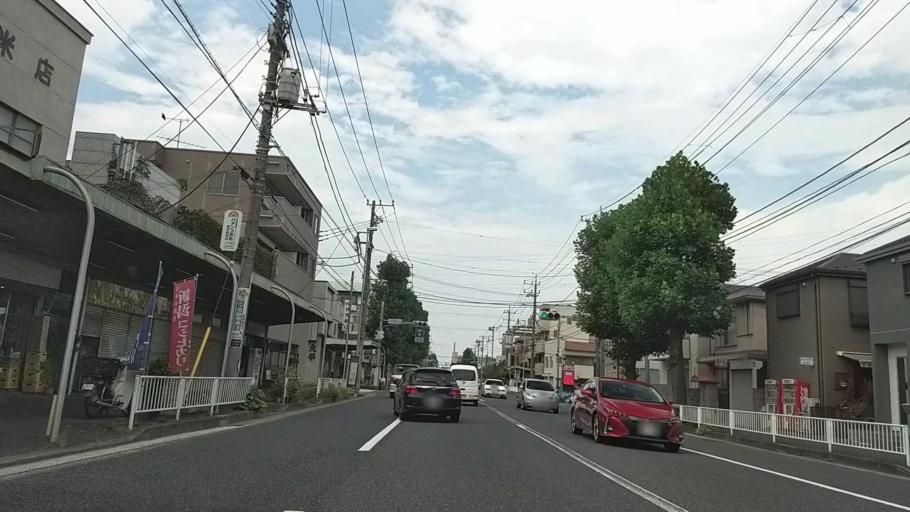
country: JP
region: Kanagawa
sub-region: Kawasaki-shi
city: Kawasaki
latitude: 35.5266
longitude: 139.6697
